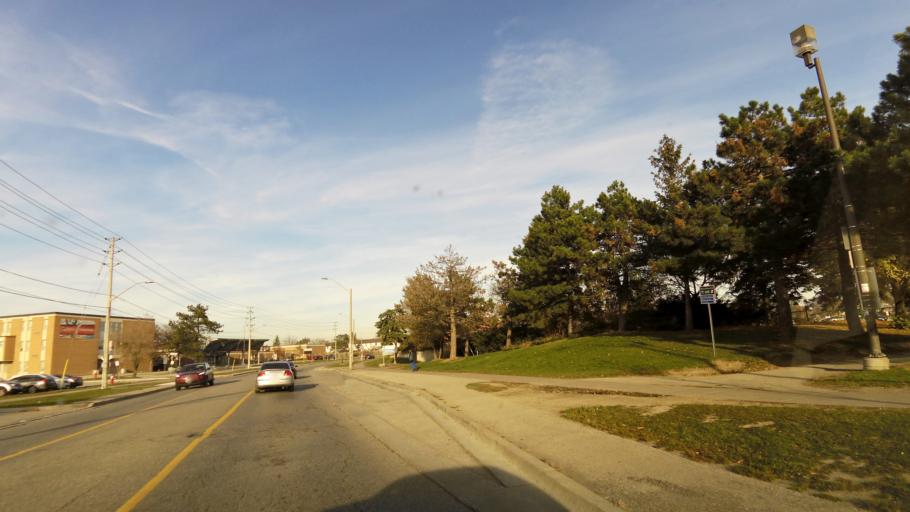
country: CA
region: Ontario
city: Etobicoke
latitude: 43.7227
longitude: -79.6404
